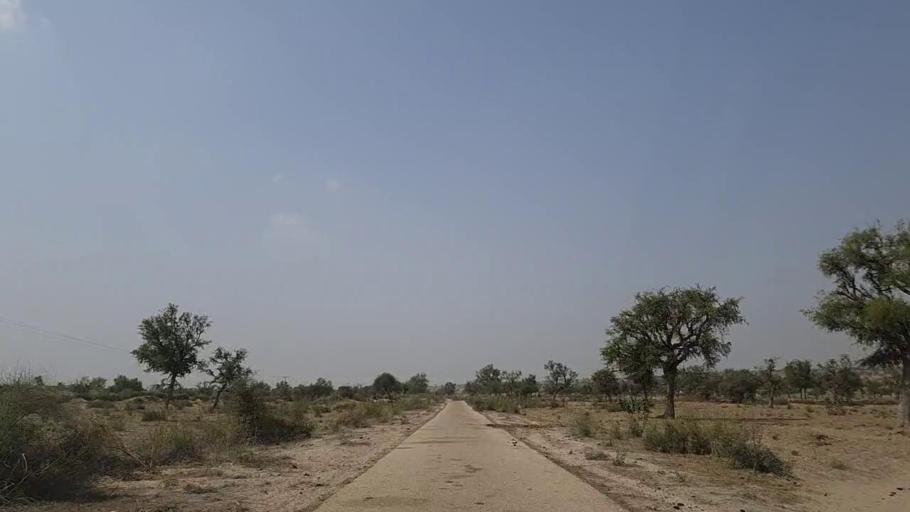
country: PK
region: Sindh
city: Mithi
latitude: 24.7643
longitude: 69.9147
